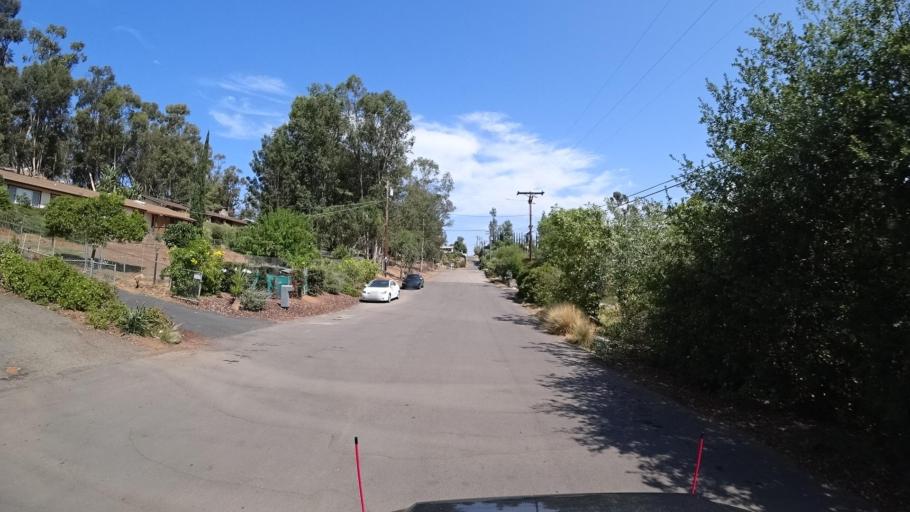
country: US
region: California
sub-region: San Diego County
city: Hidden Meadows
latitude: 33.1742
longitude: -117.0950
